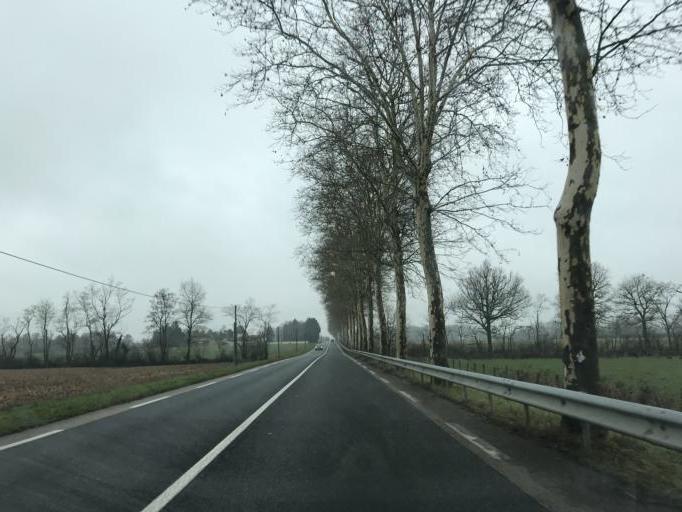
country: FR
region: Rhone-Alpes
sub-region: Departement de l'Ain
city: Saint-Paul-de-Varax
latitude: 46.0710
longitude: 5.0906
